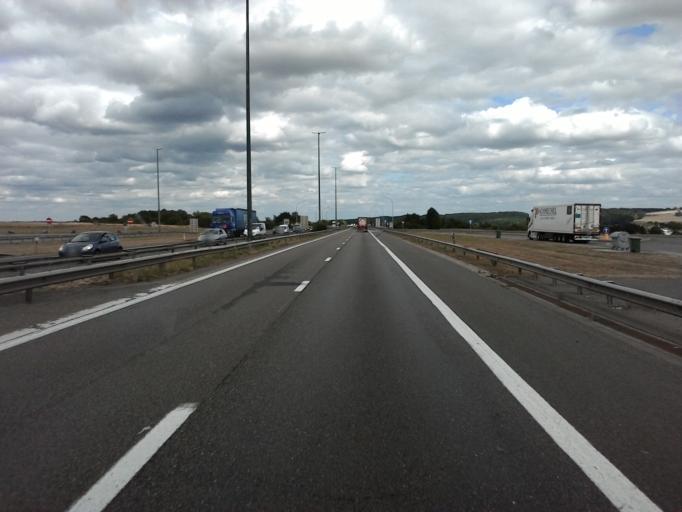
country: LU
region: Luxembourg
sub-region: Canton de Capellen
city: Steinfort
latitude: 49.6387
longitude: 5.9032
